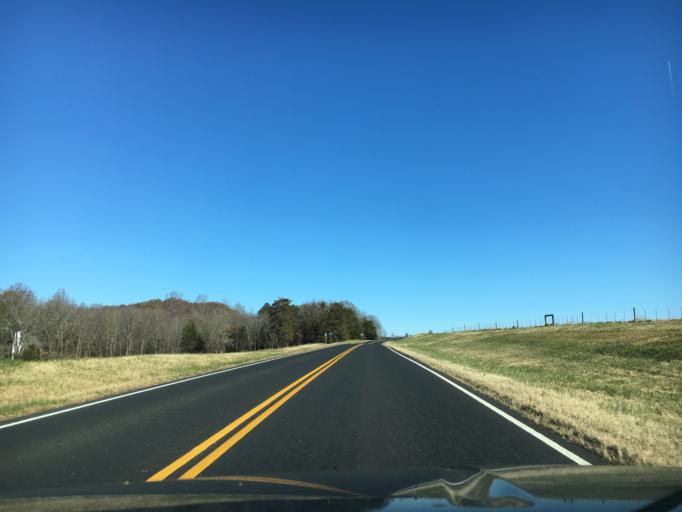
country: US
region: Virginia
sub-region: Appomattox County
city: Appomattox
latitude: 37.3842
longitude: -78.7888
